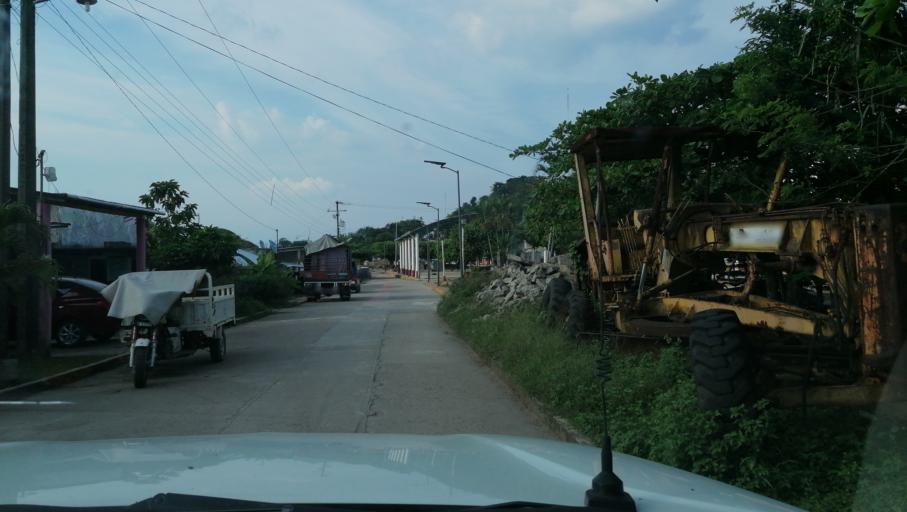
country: MX
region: Chiapas
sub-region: Juarez
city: El Triunfo 1ra. Seccion (Cardona)
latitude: 17.4881
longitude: -93.2435
